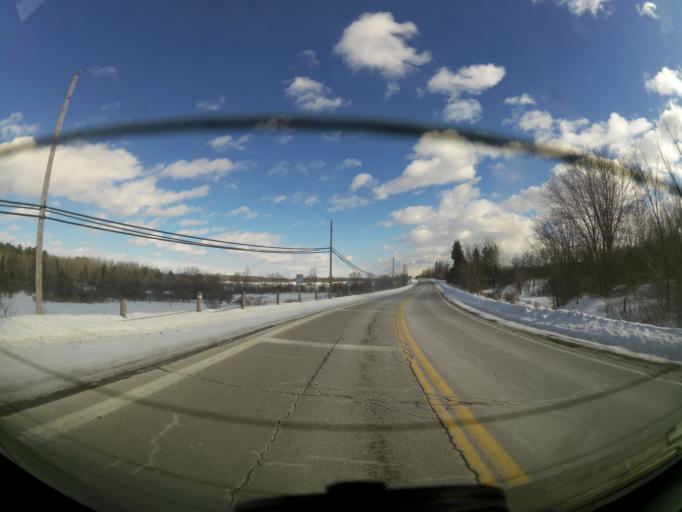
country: CA
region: Ontario
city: Ottawa
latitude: 45.3775
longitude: -75.5673
